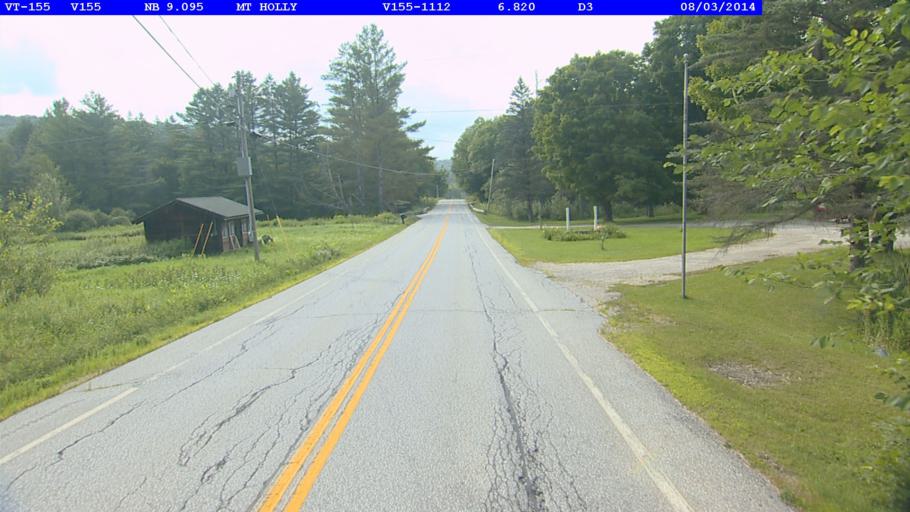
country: US
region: Vermont
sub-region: Rutland County
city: Rutland
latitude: 43.4399
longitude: -72.8626
